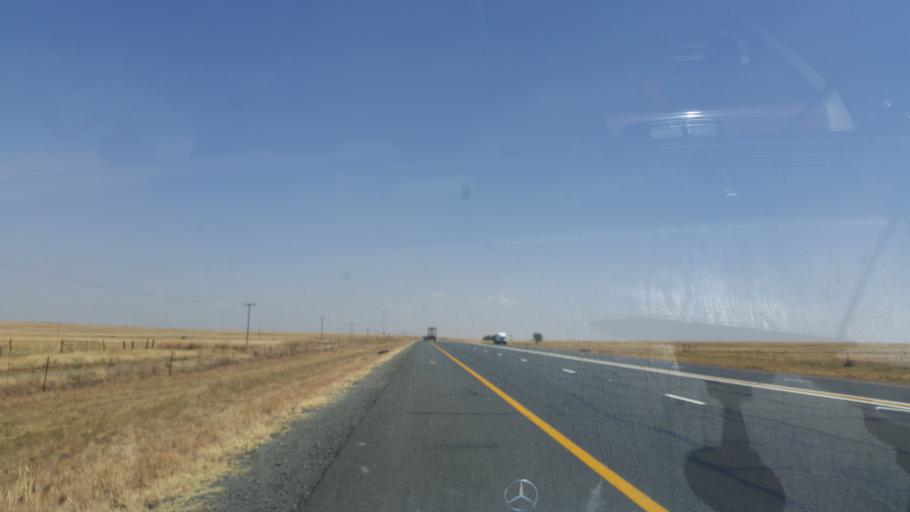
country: ZA
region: Orange Free State
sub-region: Lejweleputswa District Municipality
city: Brandfort
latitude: -28.8555
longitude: 26.5616
